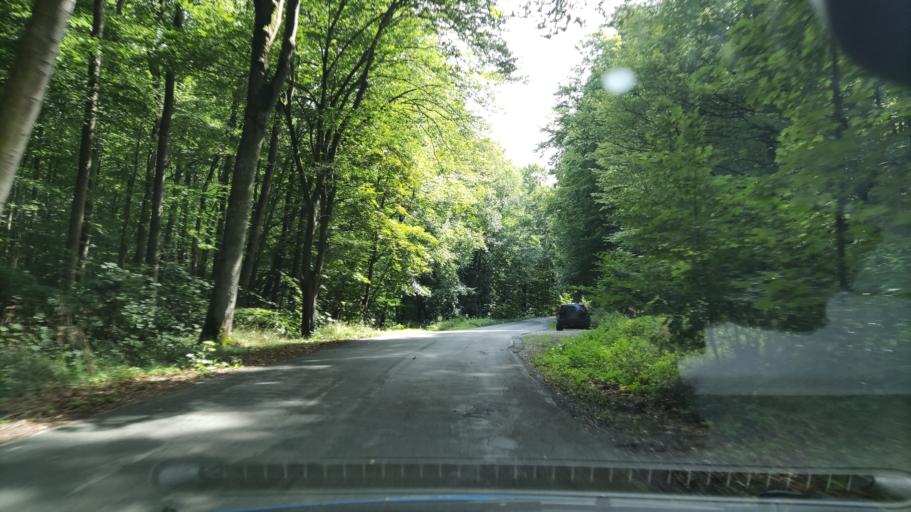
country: DE
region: Lower Saxony
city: Coppengrave
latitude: 51.9627
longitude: 9.7657
